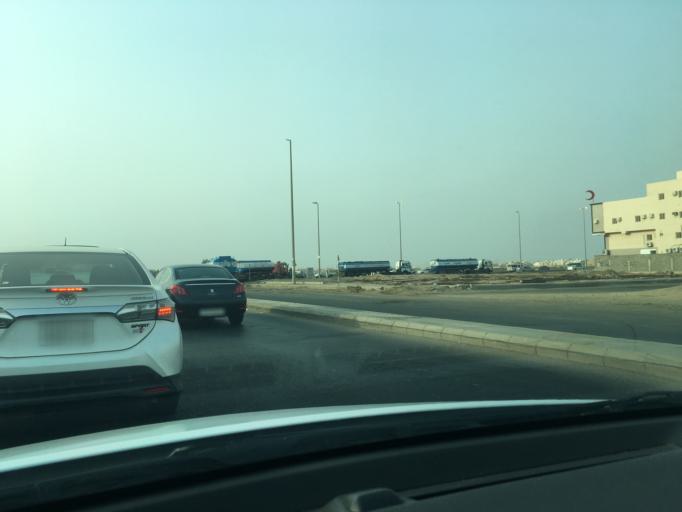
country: SA
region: Makkah
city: Jeddah
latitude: 21.7644
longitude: 39.1824
